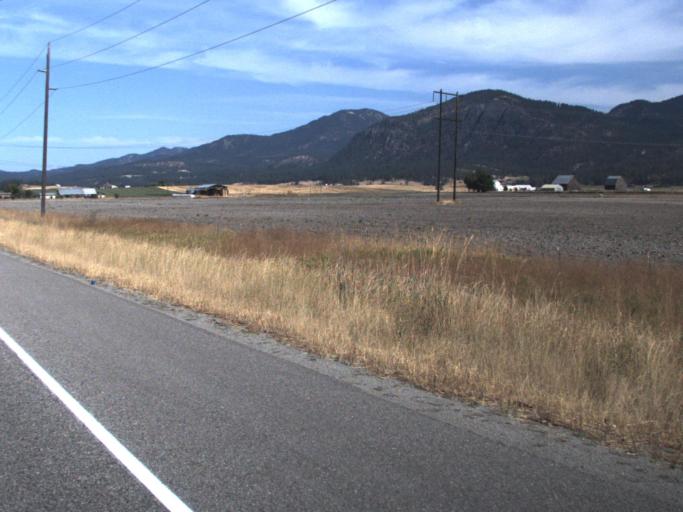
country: US
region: Washington
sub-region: Stevens County
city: Chewelah
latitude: 48.2242
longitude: -117.7153
